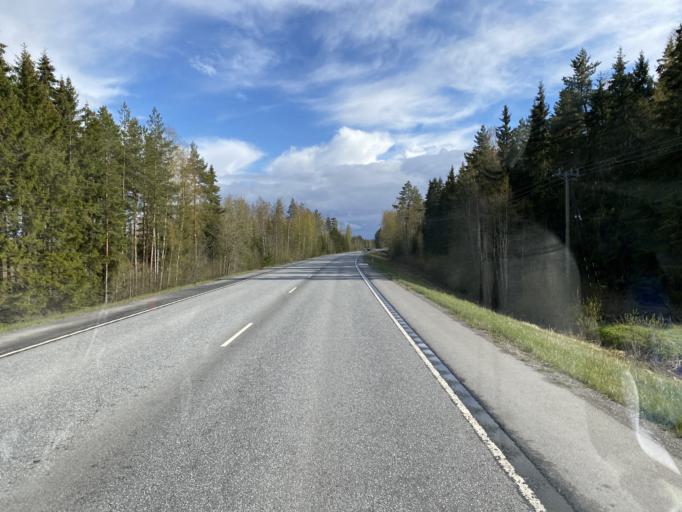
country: FI
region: Pirkanmaa
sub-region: Tampere
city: Lempaeaelae
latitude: 61.2770
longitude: 23.7468
